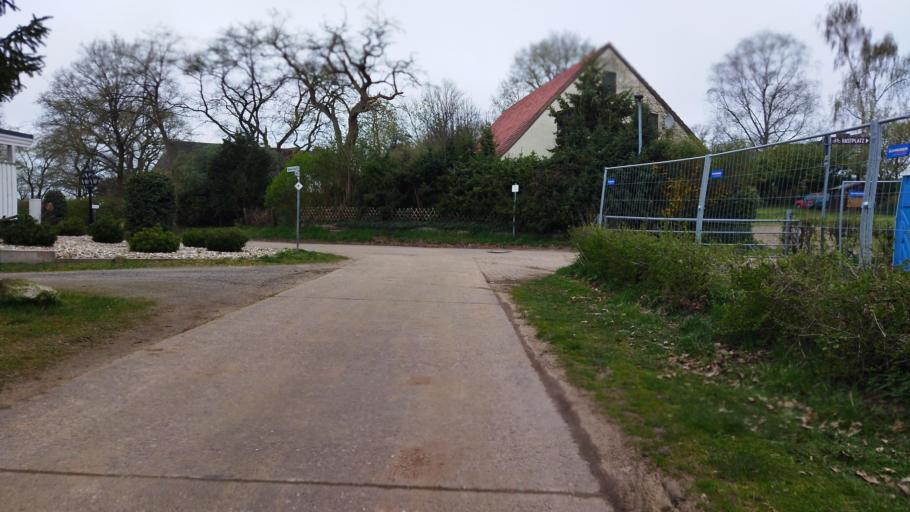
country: DE
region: Lower Saxony
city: Achim
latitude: 53.0096
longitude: 9.0103
